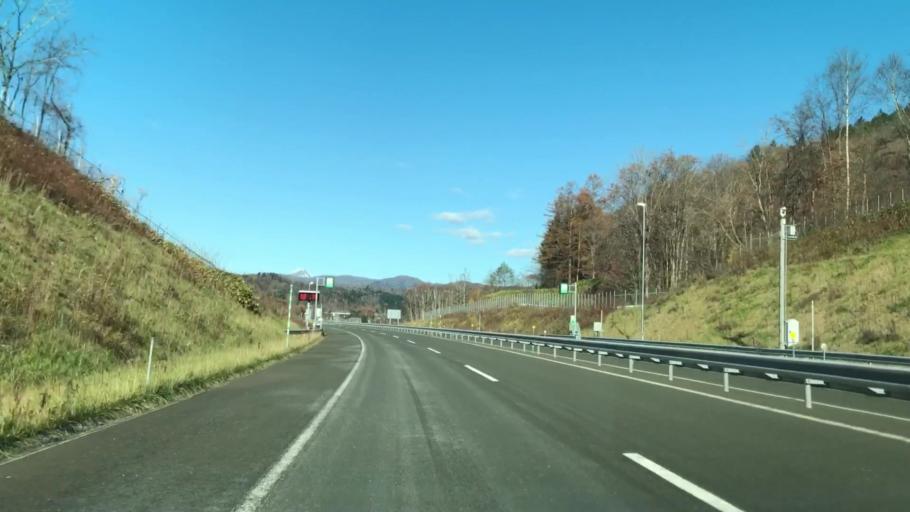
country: JP
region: Hokkaido
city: Shimo-furano
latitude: 42.9254
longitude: 142.2031
